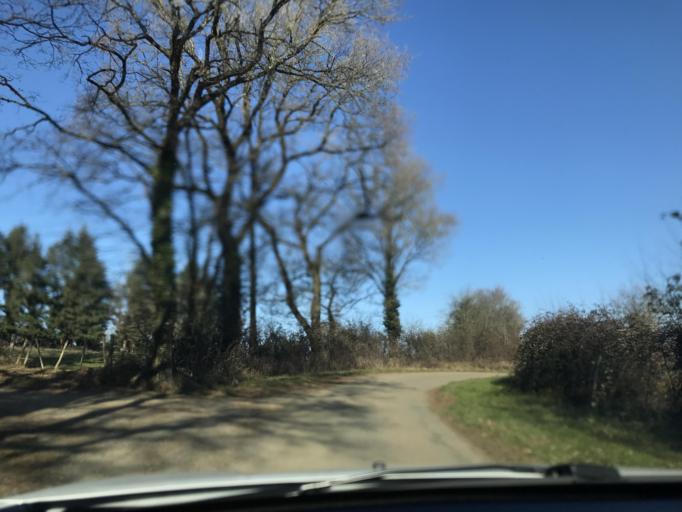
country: FR
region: Poitou-Charentes
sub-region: Departement de la Charente
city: Saint-Claud
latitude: 45.8561
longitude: 0.5296
